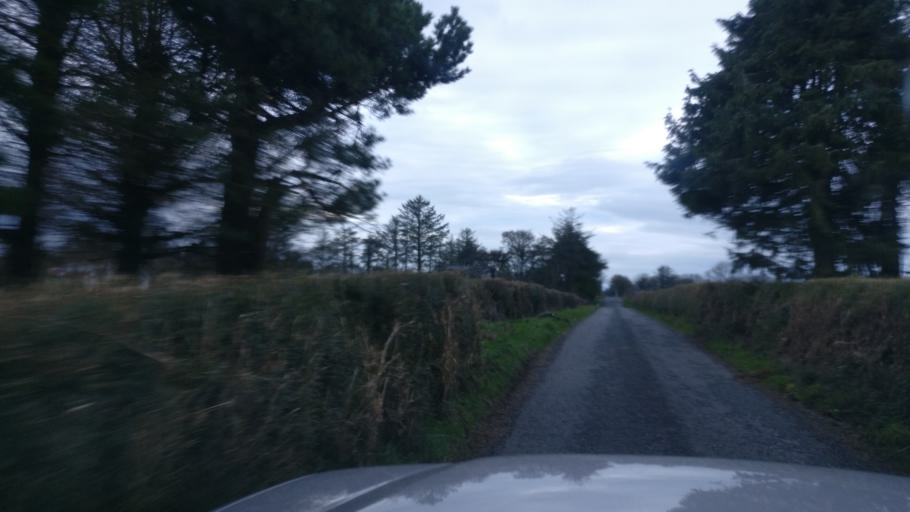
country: IE
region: Connaught
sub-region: County Galway
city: Loughrea
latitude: 53.2660
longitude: -8.4985
